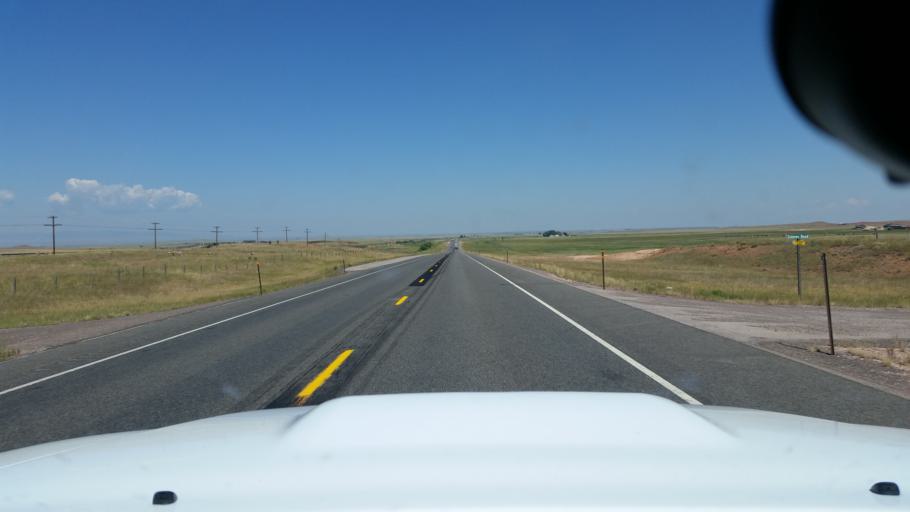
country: US
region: Wyoming
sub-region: Albany County
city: Laramie
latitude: 41.1530
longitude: -105.5713
